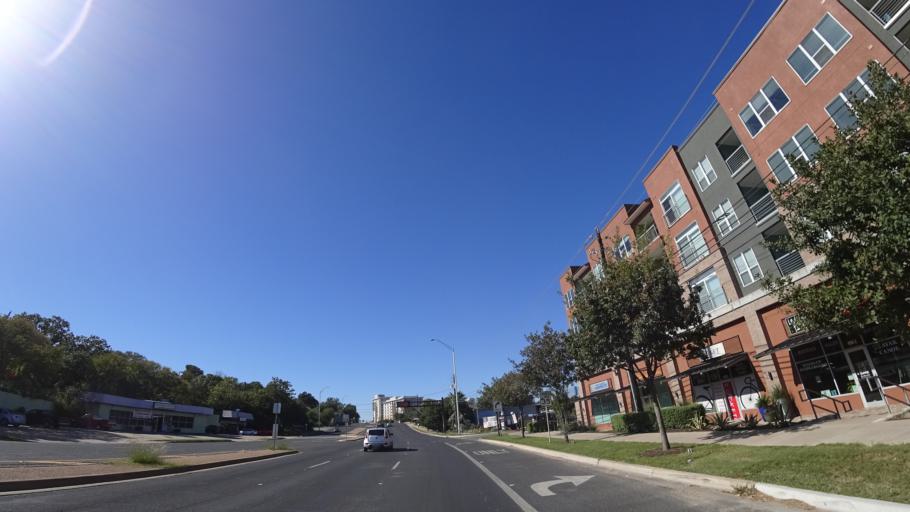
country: US
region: Texas
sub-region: Travis County
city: Austin
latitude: 30.2454
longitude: -97.7308
